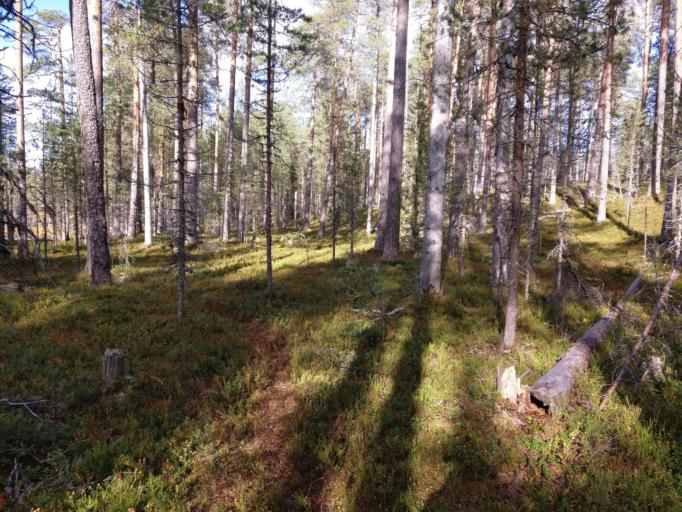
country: FI
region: Northern Savo
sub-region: Koillis-Savo
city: Rautavaara
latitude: 63.6485
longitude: 28.3032
